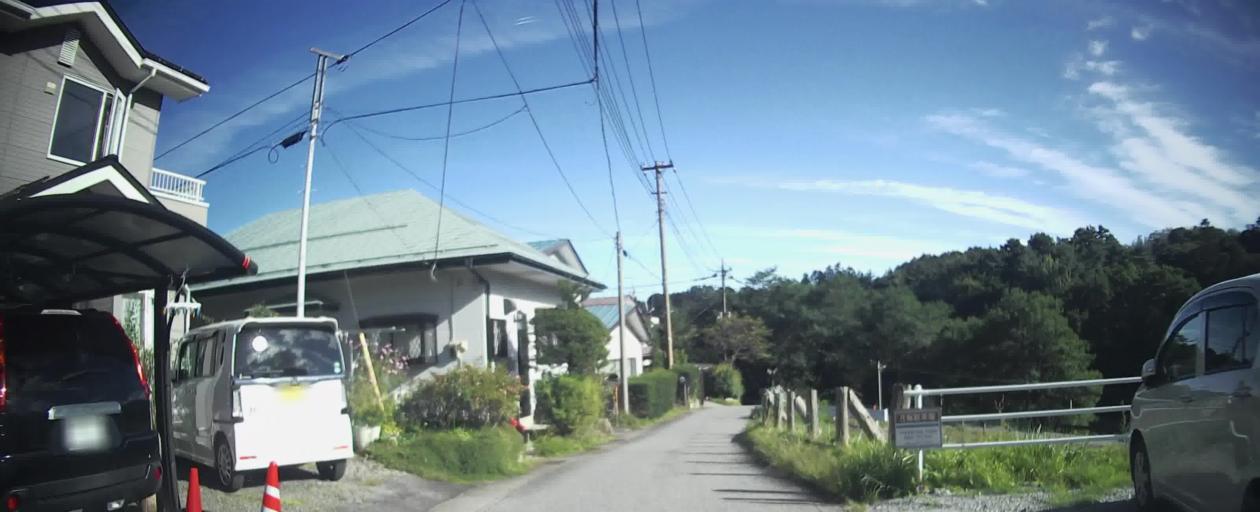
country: JP
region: Gunma
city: Nakanojomachi
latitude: 36.6238
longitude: 138.6006
